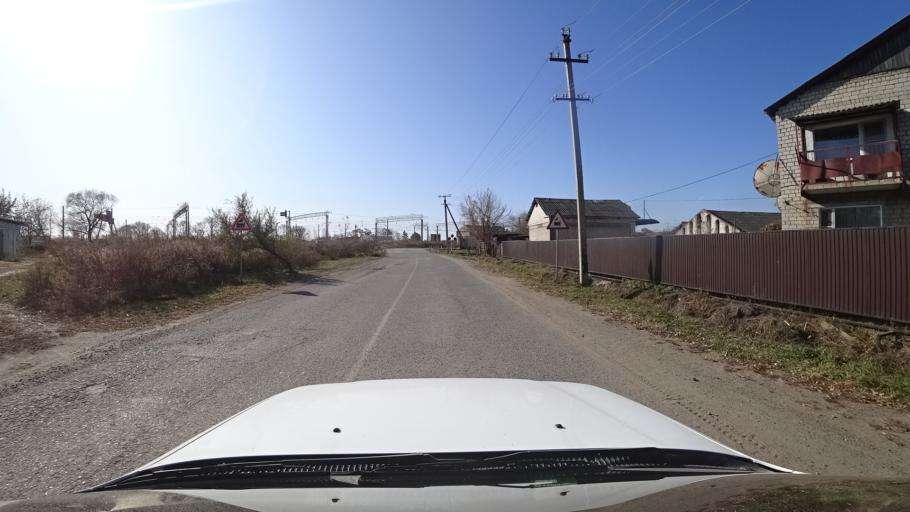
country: RU
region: Primorskiy
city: Dal'nerechensk
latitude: 45.9350
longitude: 133.7184
